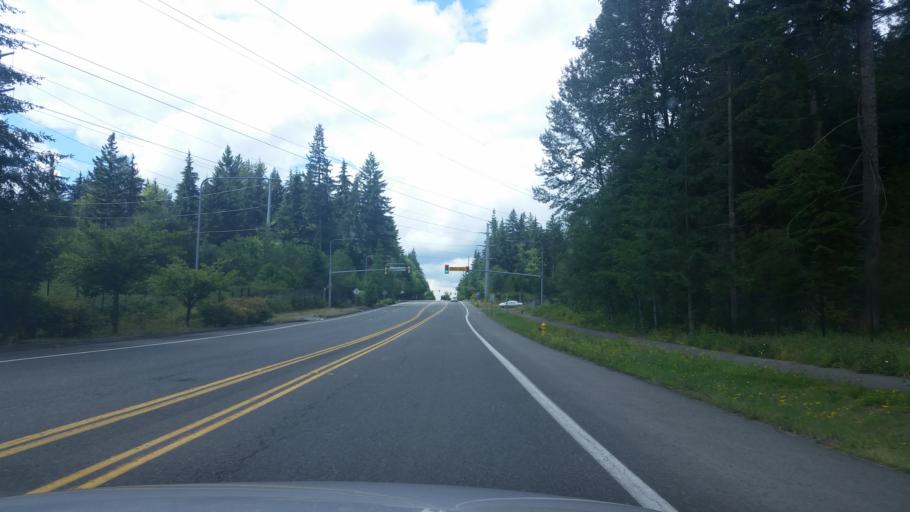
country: US
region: Washington
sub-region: King County
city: Union Hill-Novelty Hill
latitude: 47.6983
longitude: -122.0326
